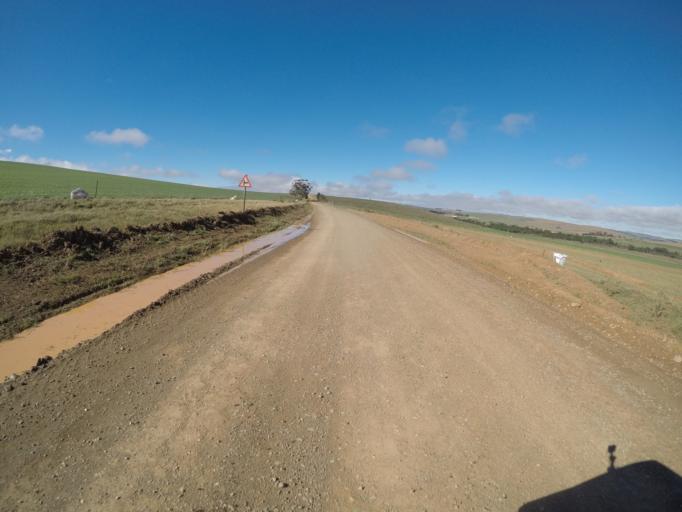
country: ZA
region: Western Cape
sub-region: Overberg District Municipality
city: Caledon
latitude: -34.1181
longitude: 19.7151
